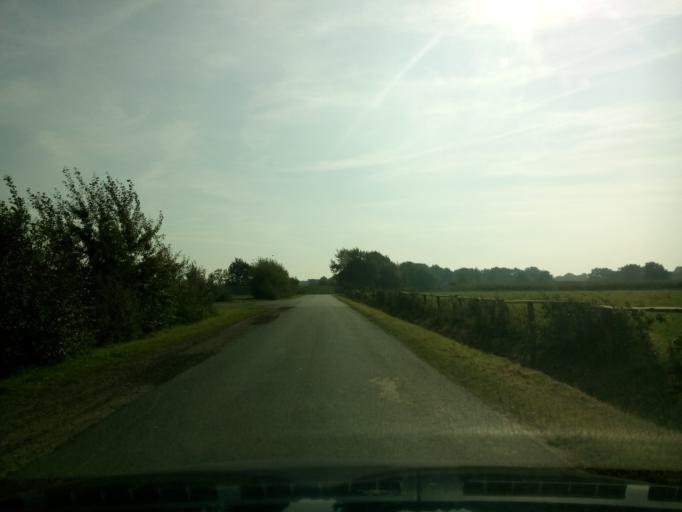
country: DE
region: Lower Saxony
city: Osterholz-Scharmbeck
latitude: 53.2485
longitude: 8.7575
